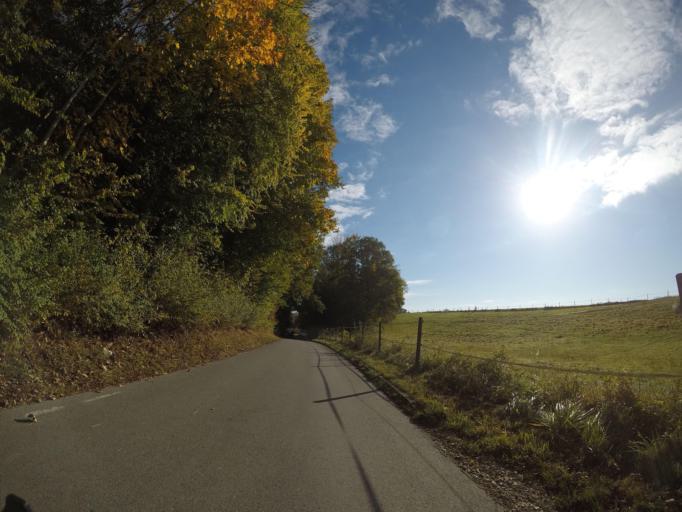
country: DE
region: Baden-Wuerttemberg
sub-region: Tuebingen Region
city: Herbertingen
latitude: 48.0450
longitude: 9.4628
